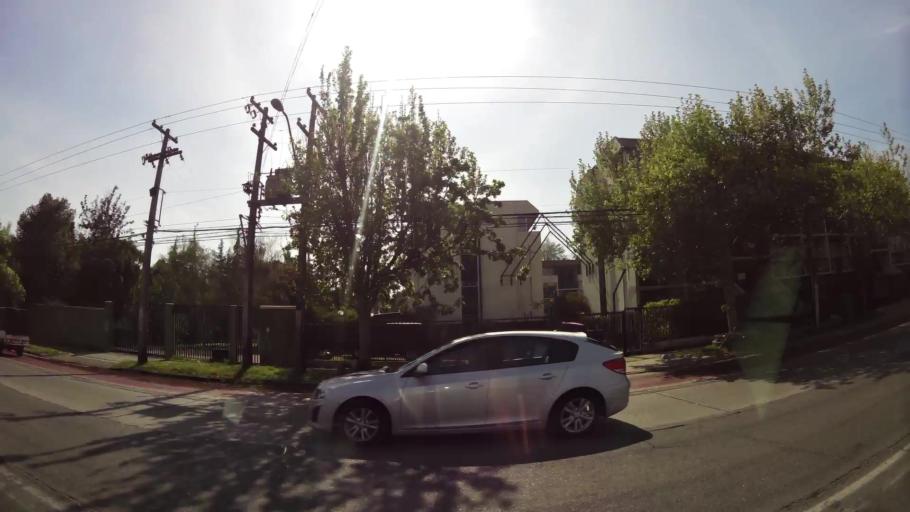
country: CL
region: Santiago Metropolitan
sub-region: Provincia de Santiago
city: Villa Presidente Frei, Nunoa, Santiago, Chile
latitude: -33.5039
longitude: -70.5929
